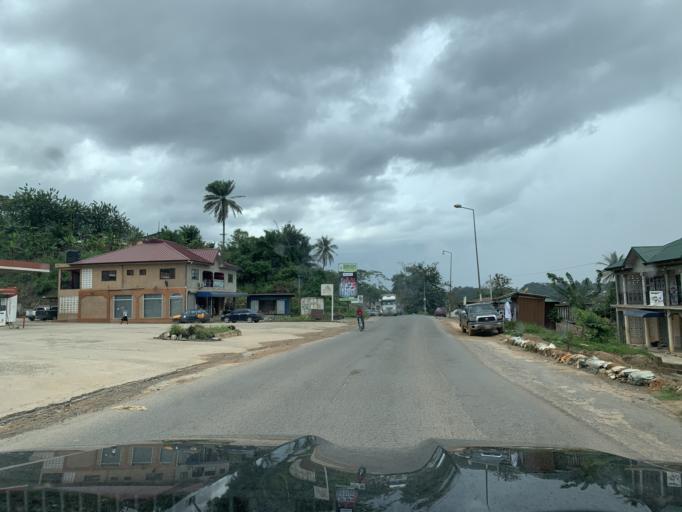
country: GH
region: Western
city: Tarkwa
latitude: 5.3154
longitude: -1.9898
